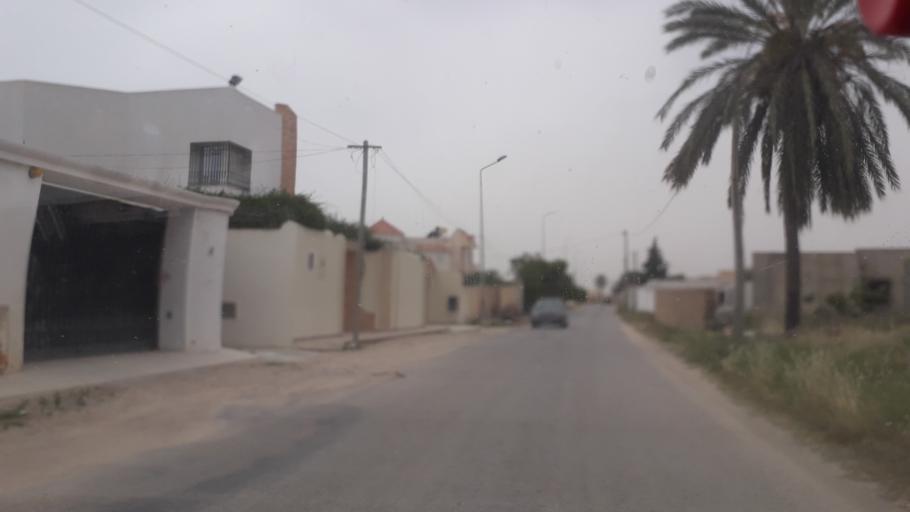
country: TN
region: Safaqis
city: Al Qarmadah
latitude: 34.7922
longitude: 10.7636
